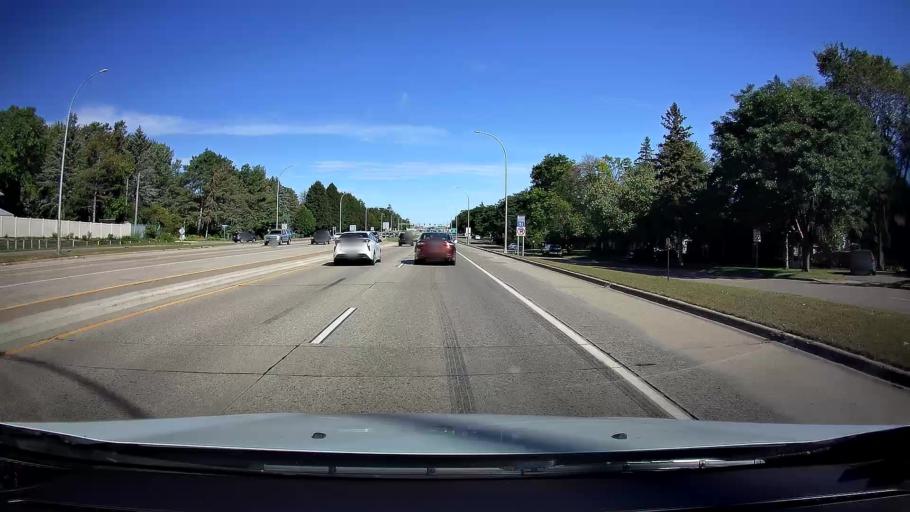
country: US
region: Minnesota
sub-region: Ramsey County
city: Falcon Heights
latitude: 44.9955
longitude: -93.1665
